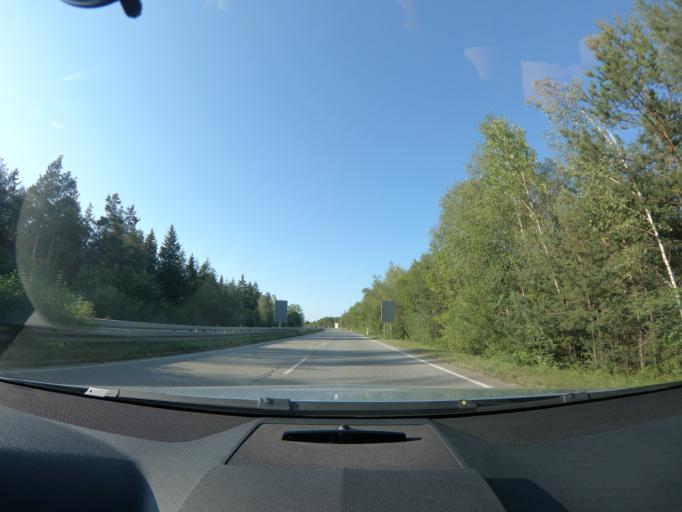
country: DE
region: Bavaria
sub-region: Upper Bavaria
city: Oberschleissheim
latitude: 48.2459
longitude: 11.6022
